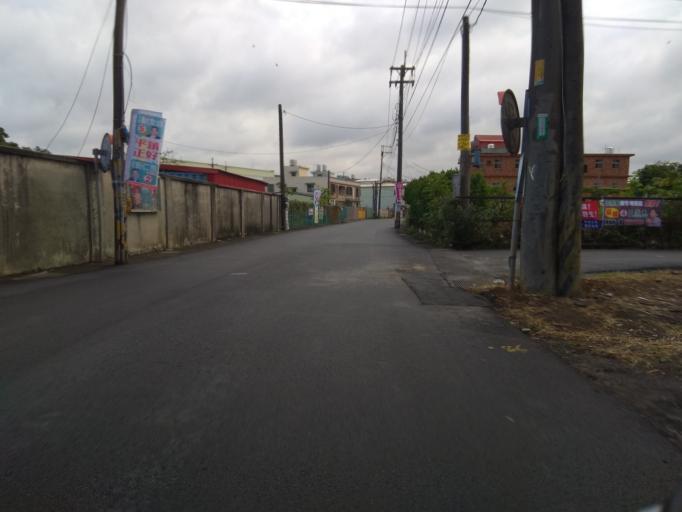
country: TW
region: Taiwan
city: Daxi
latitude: 24.9416
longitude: 121.1899
